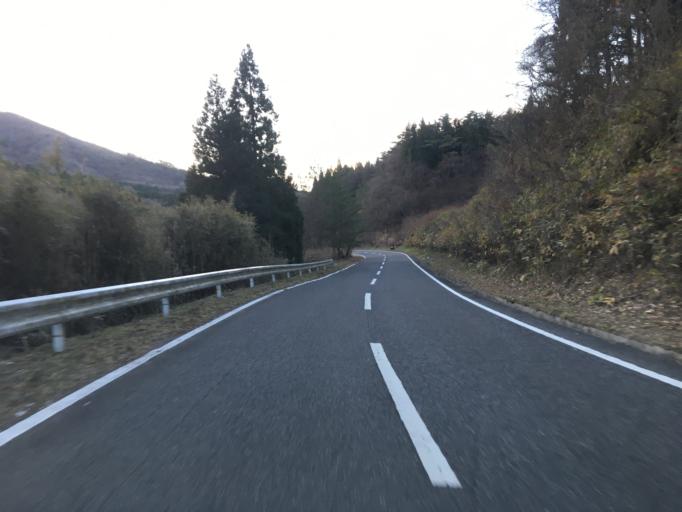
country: JP
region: Fukushima
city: Ishikawa
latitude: 37.2754
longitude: 140.5556
